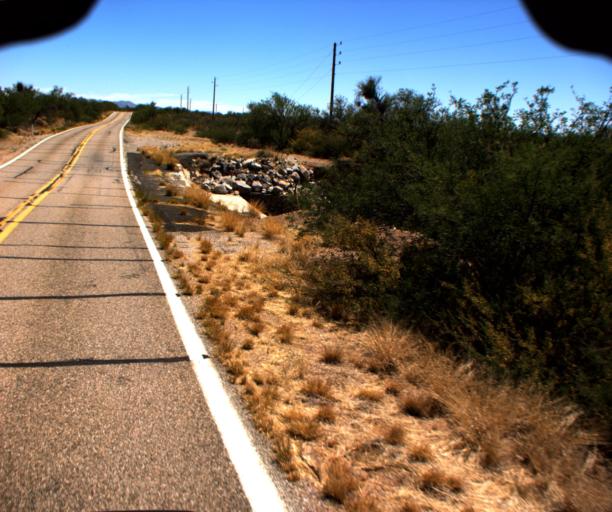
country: US
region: Arizona
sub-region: Pima County
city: Three Points
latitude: 31.8556
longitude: -111.3973
